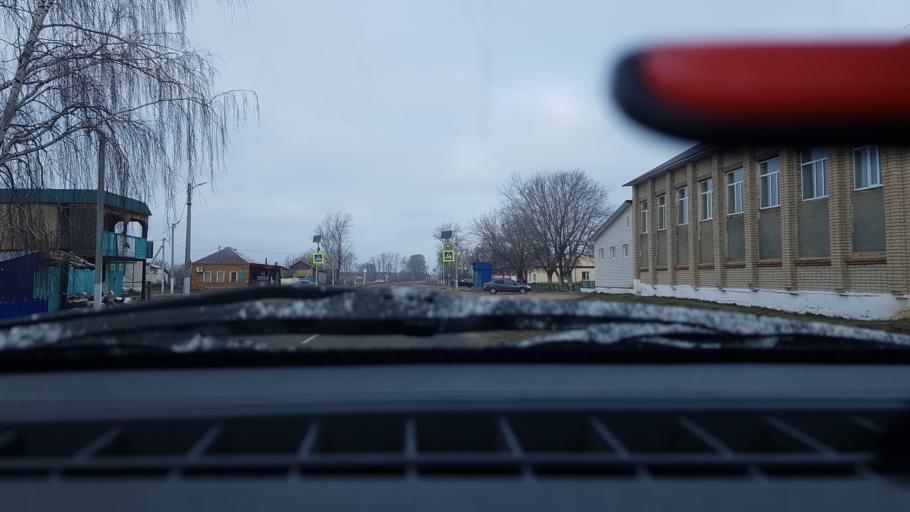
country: RU
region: Tatarstan
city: Kuybyshevskiy Zaton
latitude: 54.9120
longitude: 49.4855
